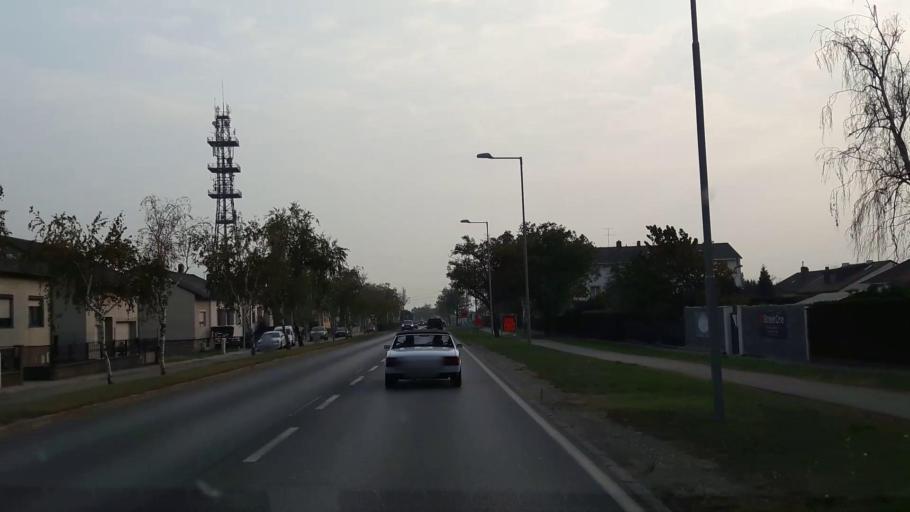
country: AT
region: Burgenland
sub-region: Politischer Bezirk Neusiedl am See
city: Neusiedl am See
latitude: 47.9643
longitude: 16.8373
